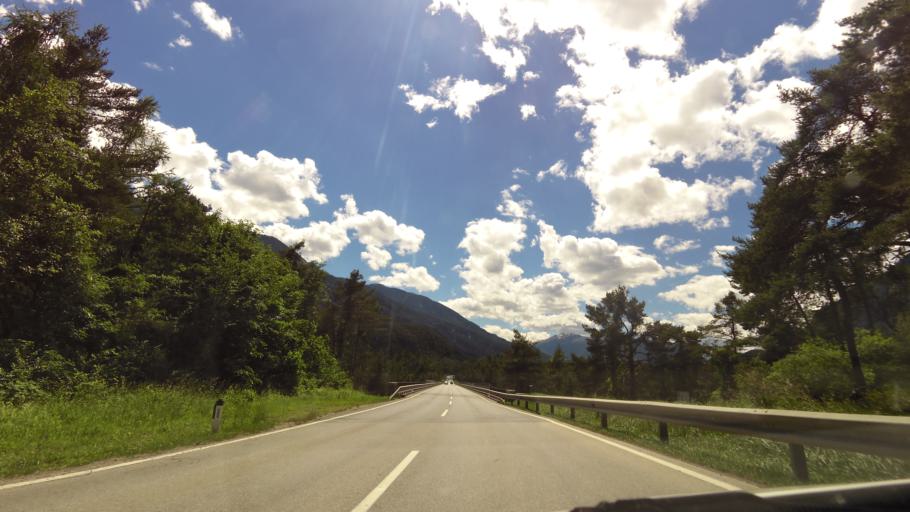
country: AT
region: Tyrol
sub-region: Politischer Bezirk Imst
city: Sautens
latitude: 47.2292
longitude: 10.8490
